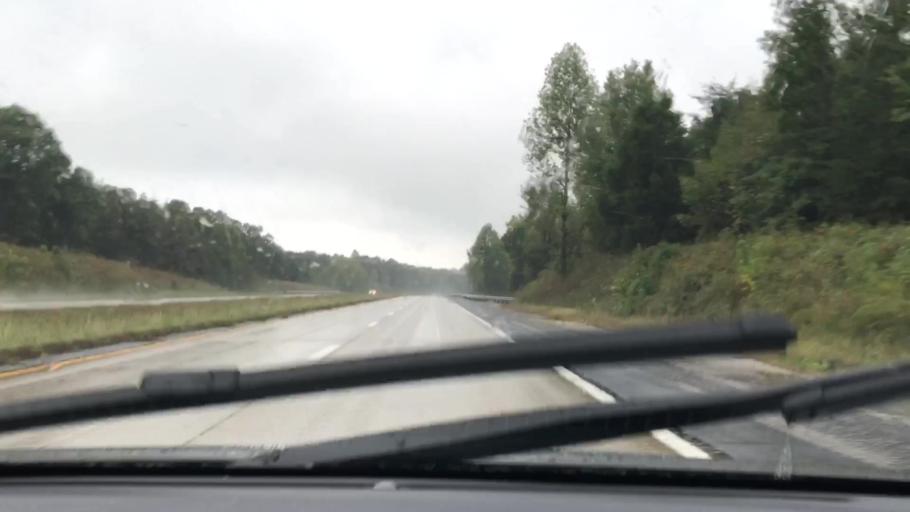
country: US
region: Kentucky
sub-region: Hopkins County
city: Nortonville
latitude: 37.1369
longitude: -87.4599
